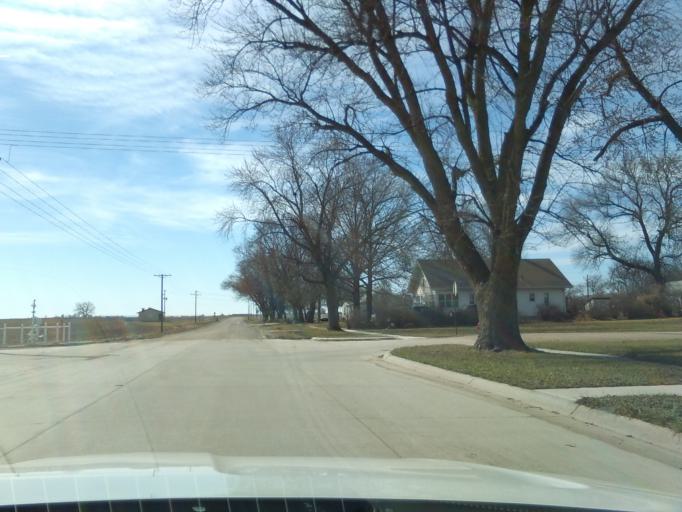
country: US
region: Nebraska
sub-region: Fillmore County
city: Geneva
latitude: 40.6312
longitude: -97.5852
